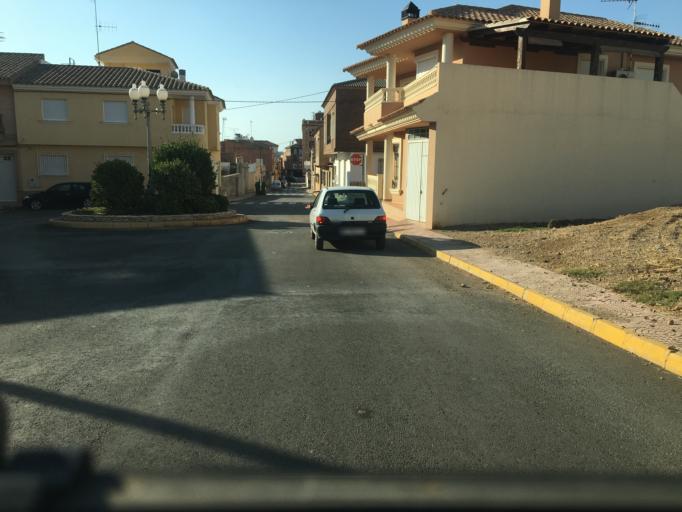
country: ES
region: Murcia
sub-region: Murcia
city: Puerto Lumbreras
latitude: 37.5671
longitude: -1.8068
